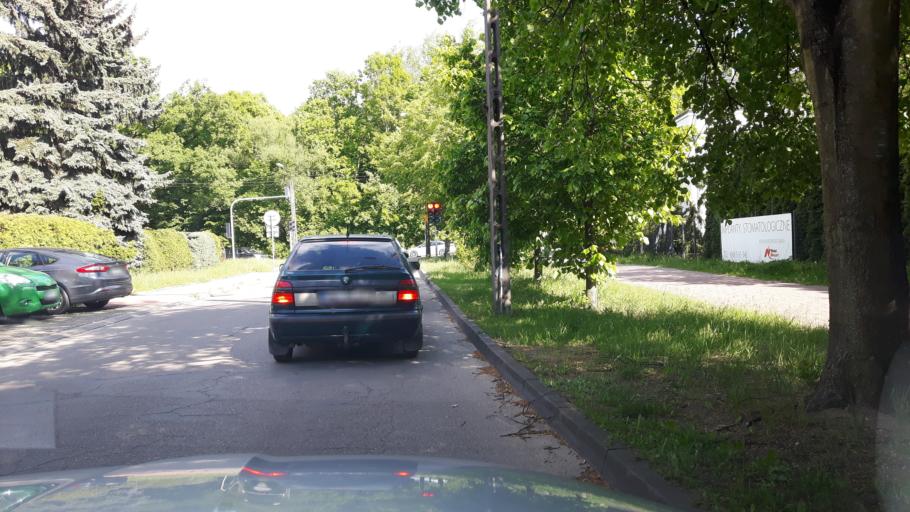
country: PL
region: Masovian Voivodeship
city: Zielonka
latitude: 52.3141
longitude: 21.1544
